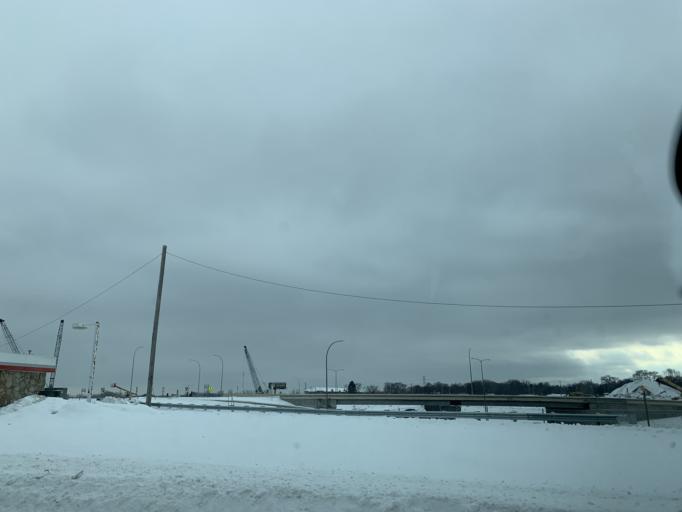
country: US
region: Minnesota
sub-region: Ramsey County
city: Little Canada
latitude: 45.0469
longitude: -93.1079
